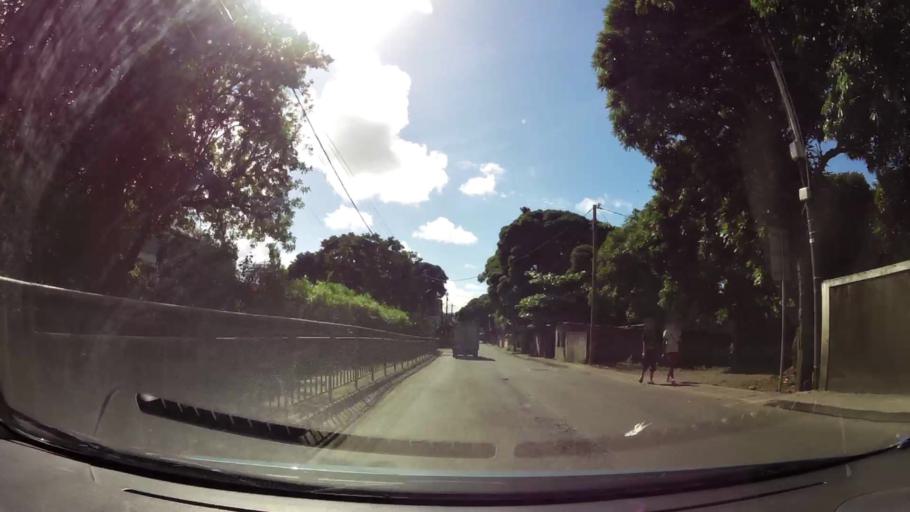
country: MU
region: Grand Port
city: Plaine Magnien
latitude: -20.4335
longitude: 57.6598
